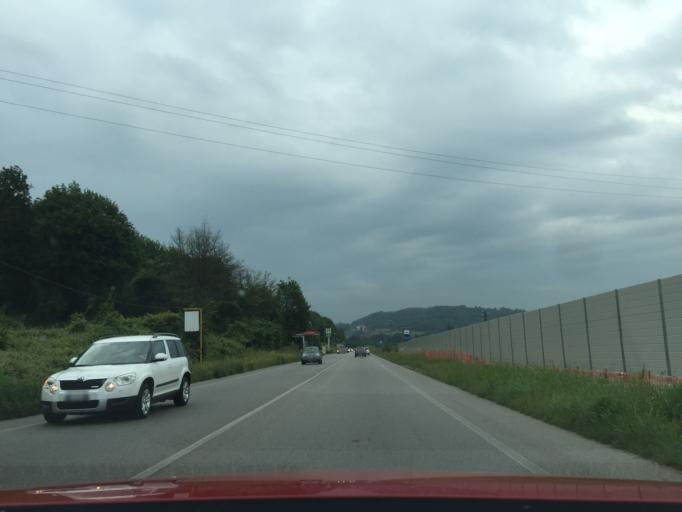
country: IT
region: Tuscany
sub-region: Provincia di Pistoia
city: Serravalle Pistoiese
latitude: 43.9082
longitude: 10.8420
